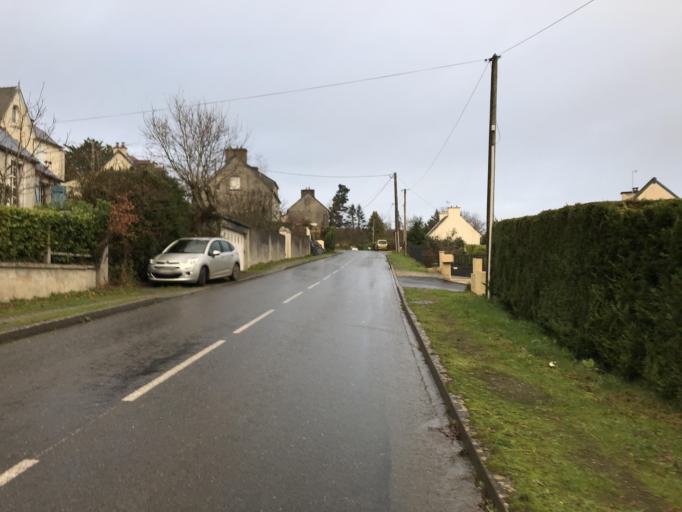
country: FR
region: Brittany
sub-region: Departement du Finistere
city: Loperhet
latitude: 48.3663
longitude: -4.3090
